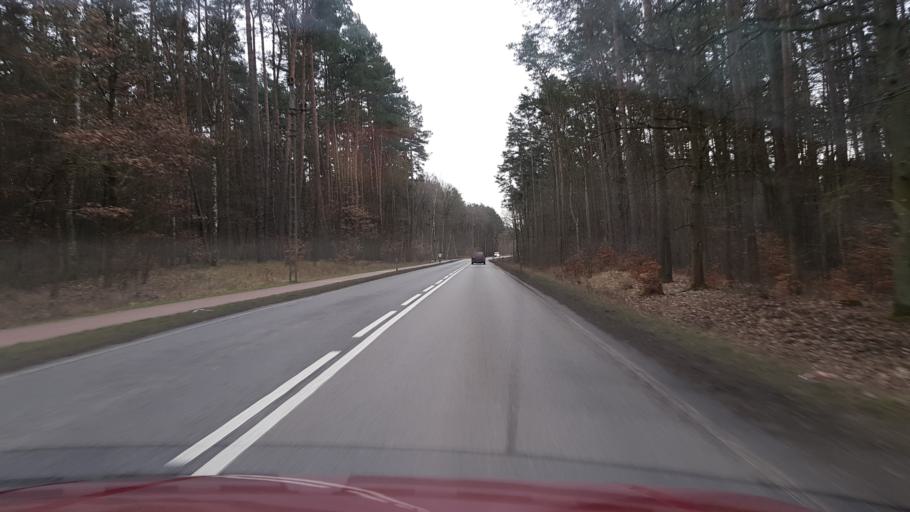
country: PL
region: West Pomeranian Voivodeship
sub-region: Powiat policki
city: Dobra
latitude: 53.5158
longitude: 14.4724
